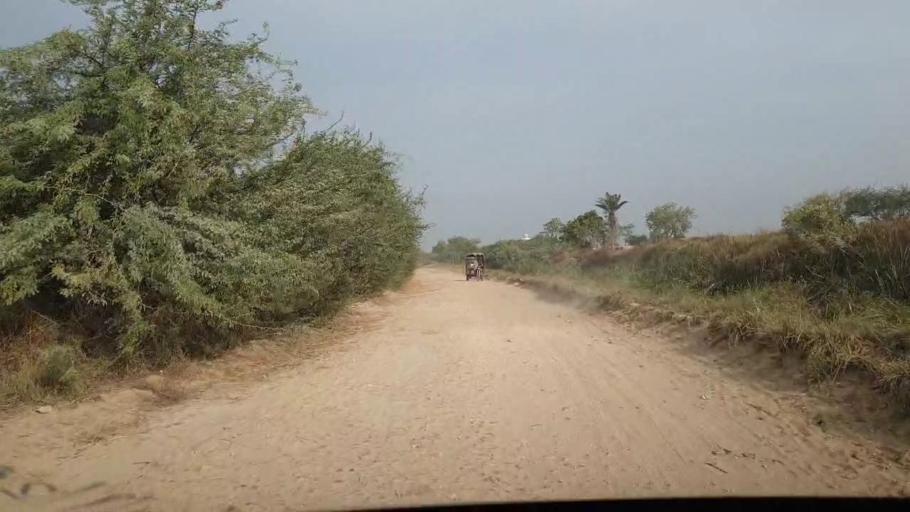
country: PK
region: Sindh
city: Chuhar Jamali
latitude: 24.3937
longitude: 67.9740
